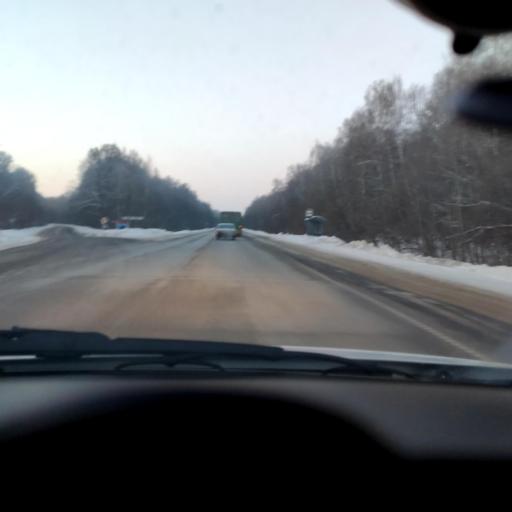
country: RU
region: Kursk
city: Zheleznogorsk
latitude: 52.2884
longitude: 35.3238
